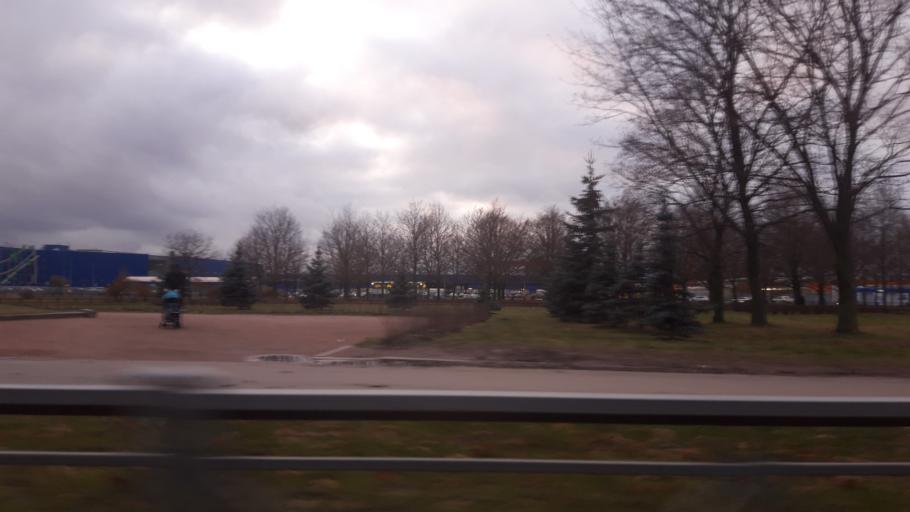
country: RU
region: St.-Petersburg
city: Kupchino
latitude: 59.8230
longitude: 30.3225
